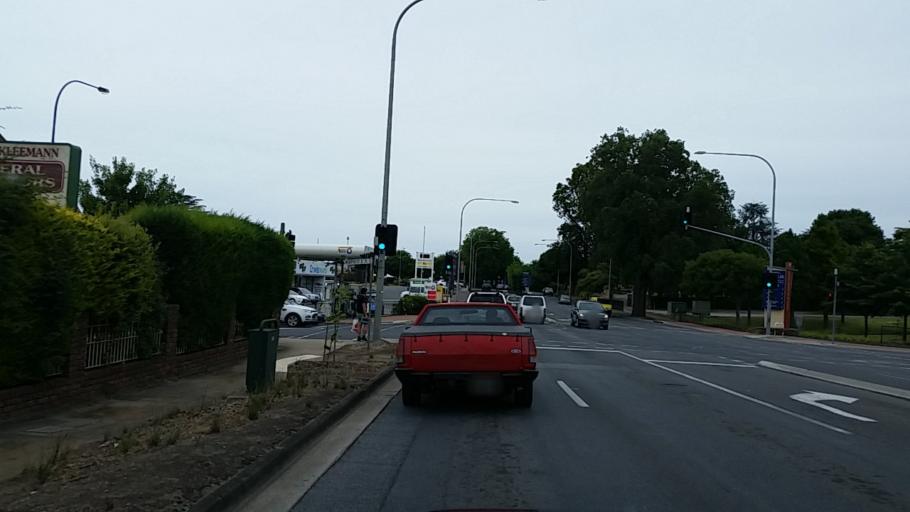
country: AU
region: South Australia
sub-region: Mount Barker
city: Mount Barker
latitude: -35.0663
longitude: 138.8561
